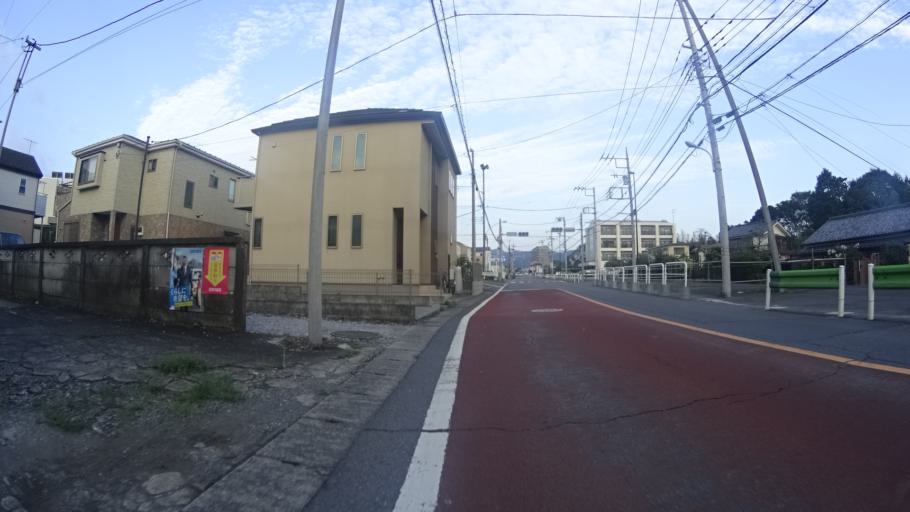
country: JP
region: Tokyo
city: Ome
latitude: 35.7806
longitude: 139.2693
